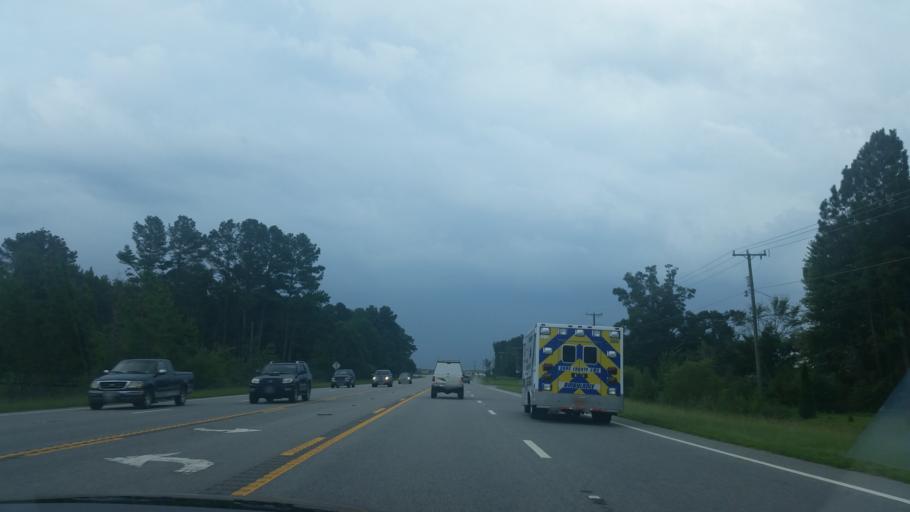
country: US
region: North Carolina
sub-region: Currituck County
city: Currituck
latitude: 36.4652
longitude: -76.1044
